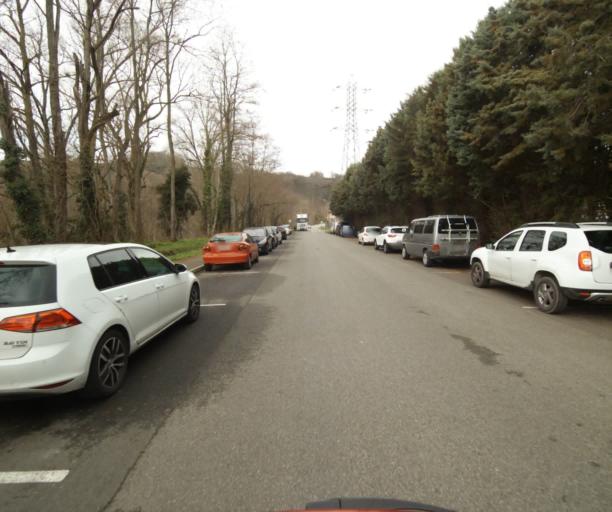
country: FR
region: Midi-Pyrenees
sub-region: Departement de l'Ariege
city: Pamiers
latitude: 43.1178
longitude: 1.6009
